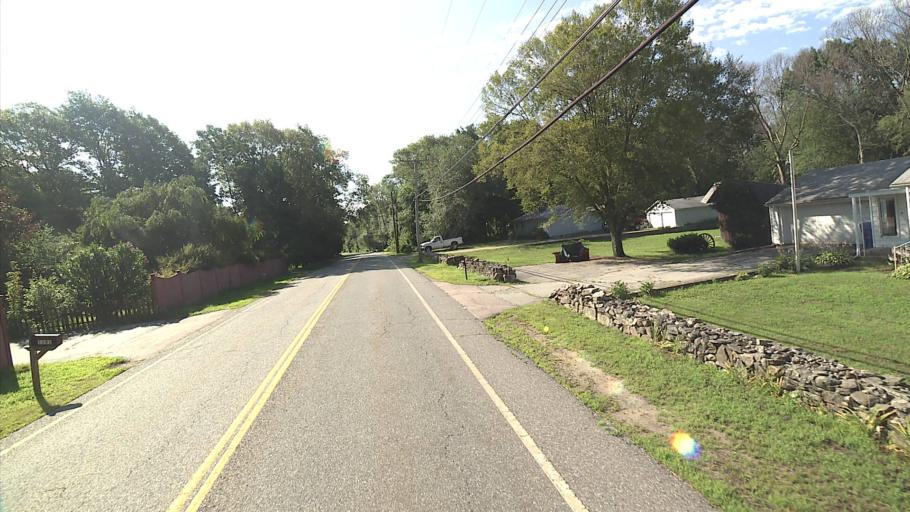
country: US
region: Connecticut
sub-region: New London County
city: Montville Center
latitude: 41.4912
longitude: -72.1750
